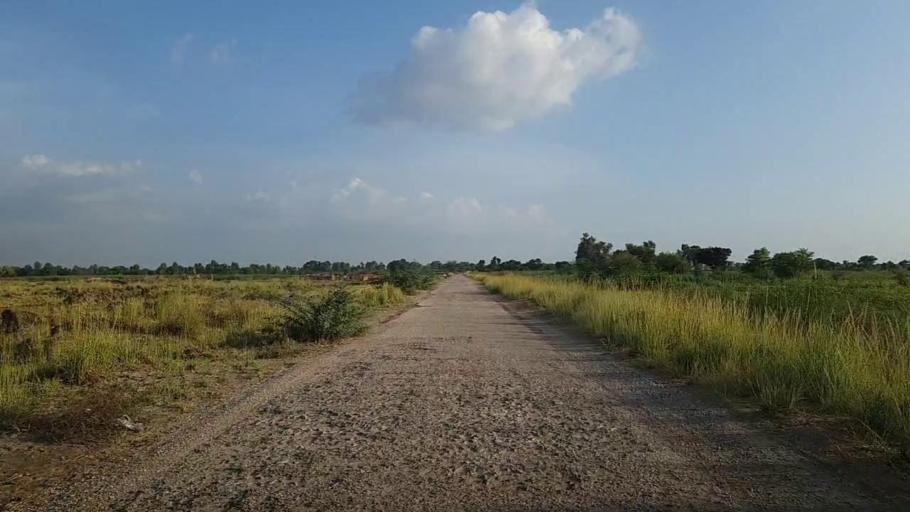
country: PK
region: Sindh
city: Hingorja
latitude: 27.0682
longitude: 68.4188
